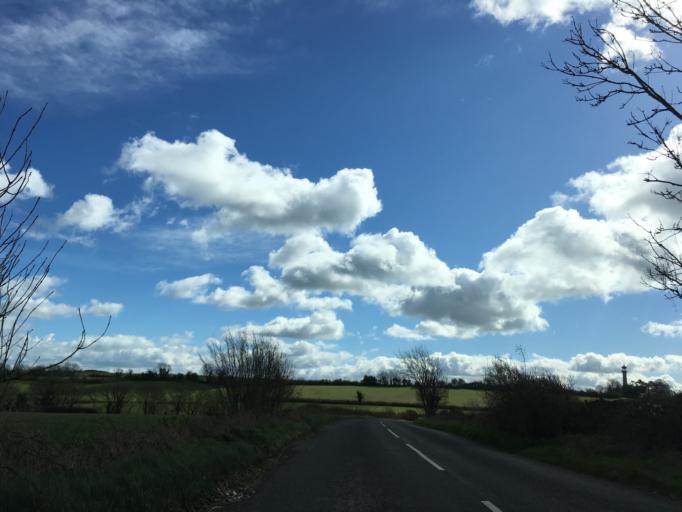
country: GB
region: England
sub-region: South Gloucestershire
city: Horton
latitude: 51.5927
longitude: -2.3344
